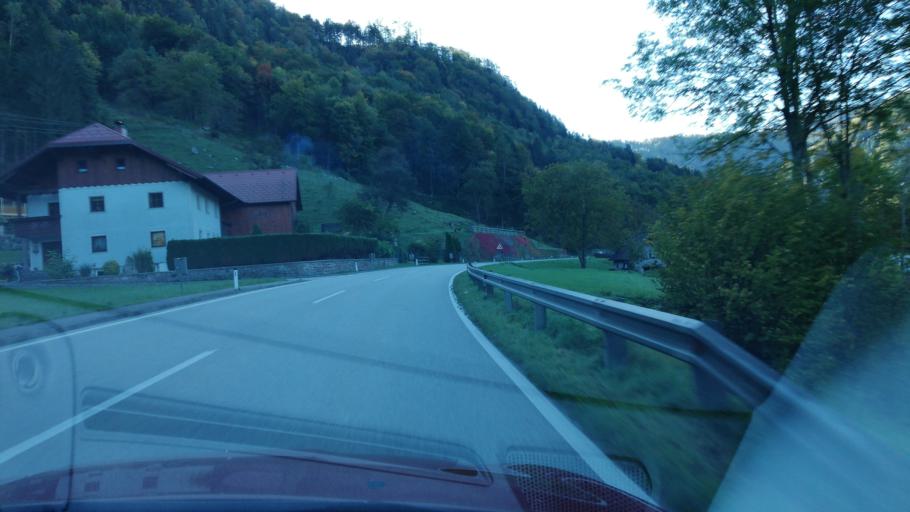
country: AT
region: Upper Austria
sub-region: Politischer Bezirk Steyr-Land
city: Losenstein
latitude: 47.9105
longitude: 14.4505
